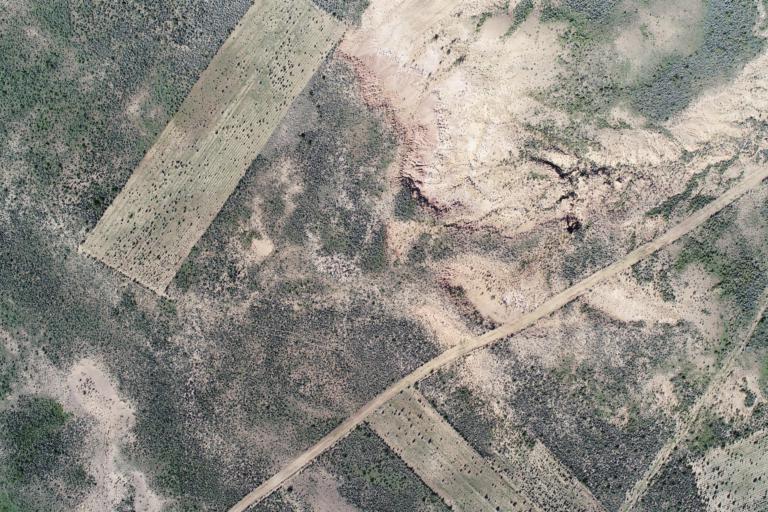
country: BO
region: La Paz
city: Curahuara de Carangas
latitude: -17.3025
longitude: -68.5166
